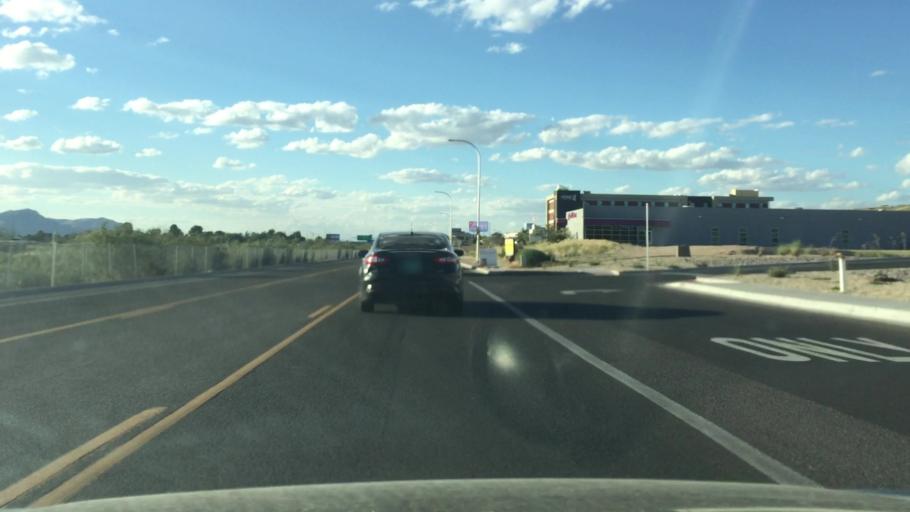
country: US
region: New Mexico
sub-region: Dona Ana County
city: Las Cruces
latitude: 32.3339
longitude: -106.7592
